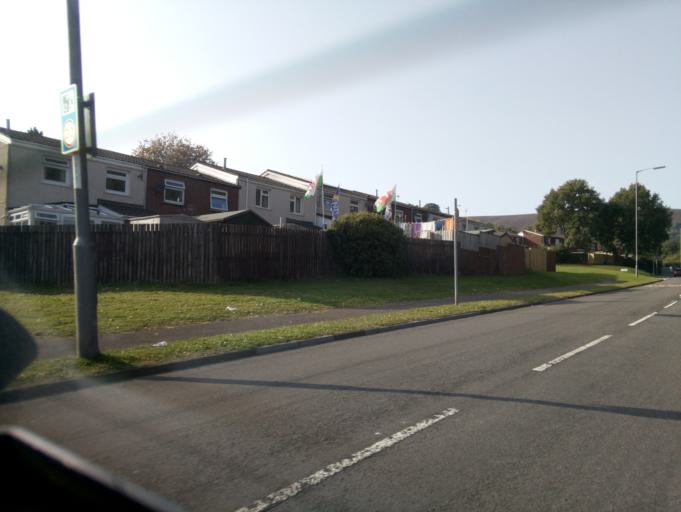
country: GB
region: Wales
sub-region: Torfaen County Borough
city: Cwmbran
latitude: 51.6601
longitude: -3.0454
